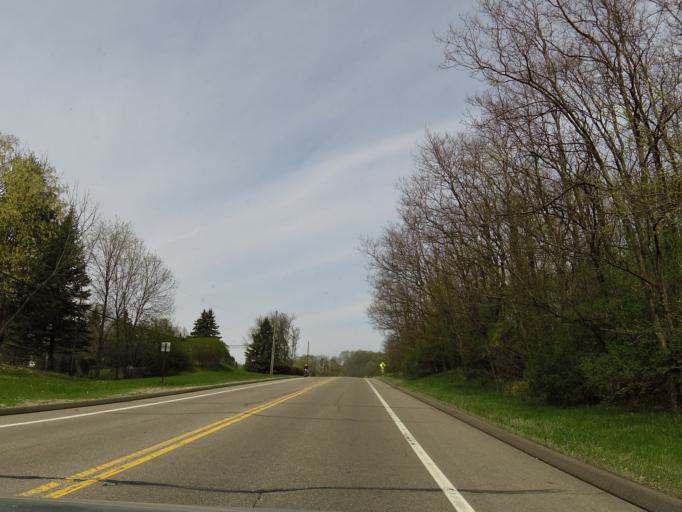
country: US
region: Minnesota
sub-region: Scott County
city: Savage
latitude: 44.8219
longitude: -93.3788
